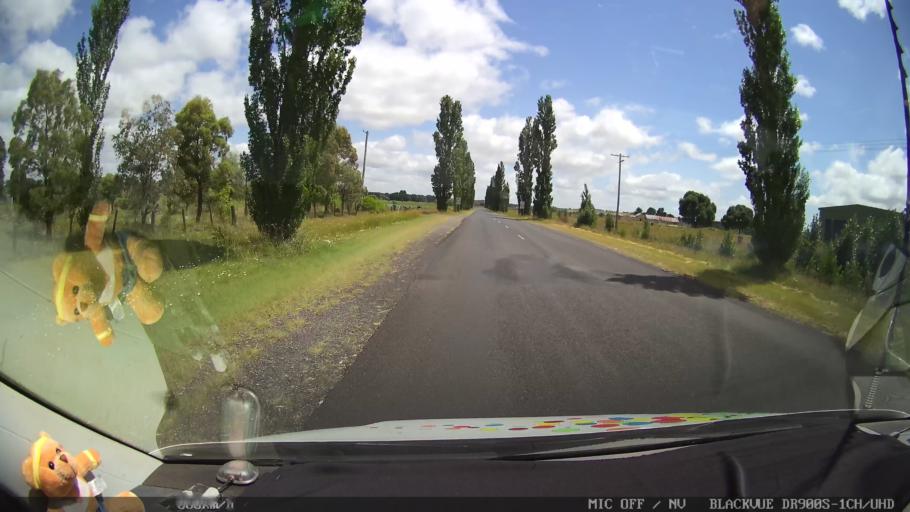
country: AU
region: New South Wales
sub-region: Glen Innes Severn
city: Glen Innes
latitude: -29.7235
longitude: 151.7262
